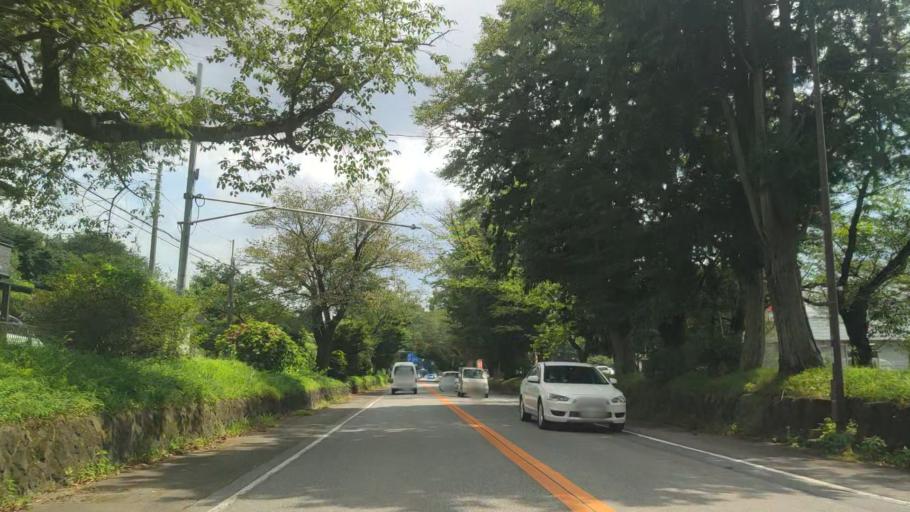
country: JP
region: Tochigi
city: Utsunomiya-shi
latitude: 36.6304
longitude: 139.8512
